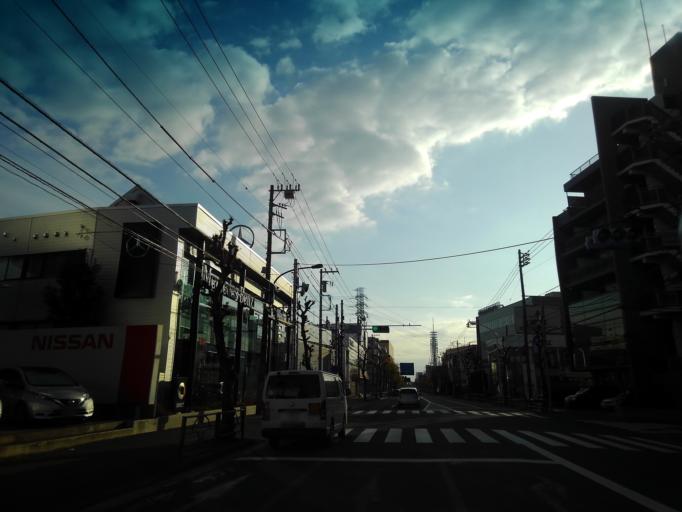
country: JP
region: Tokyo
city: Tanashicho
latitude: 35.7396
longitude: 139.5078
